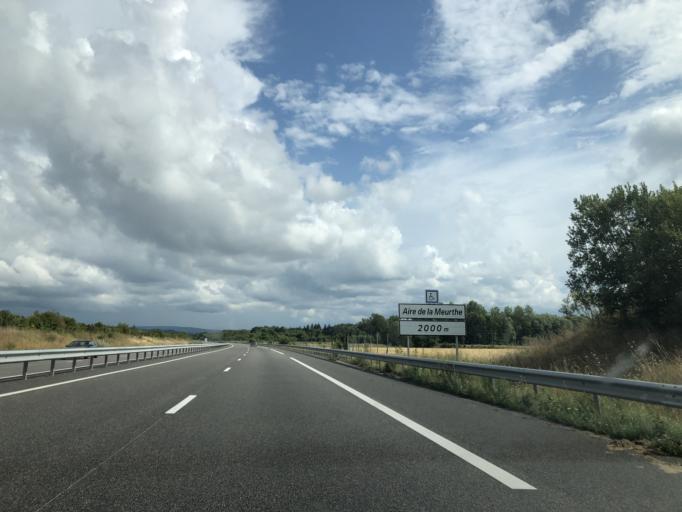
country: FR
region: Lorraine
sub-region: Departement de Meurthe-et-Moselle
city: Baccarat
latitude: 48.4829
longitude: 6.7116
